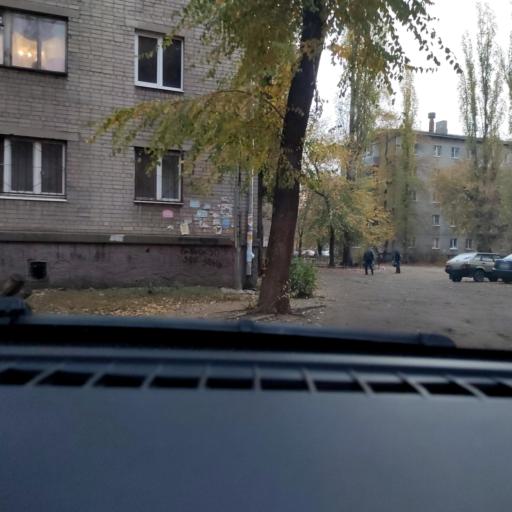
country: RU
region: Voronezj
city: Maslovka
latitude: 51.6343
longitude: 39.2661
